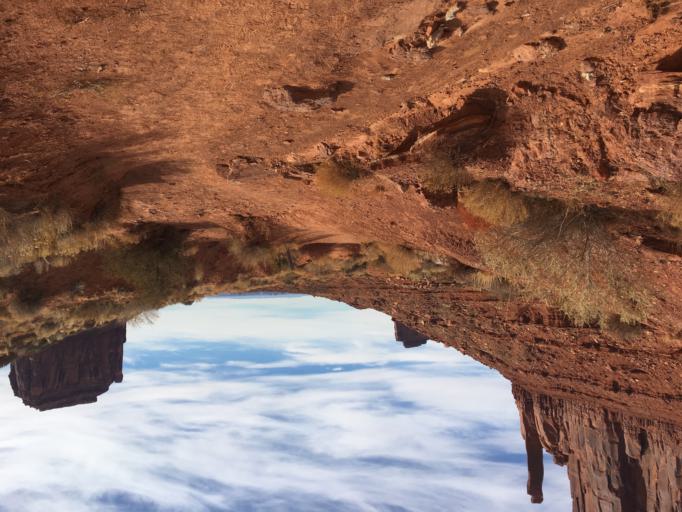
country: US
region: Arizona
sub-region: Navajo County
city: Kayenta
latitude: 36.9884
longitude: -110.1026
